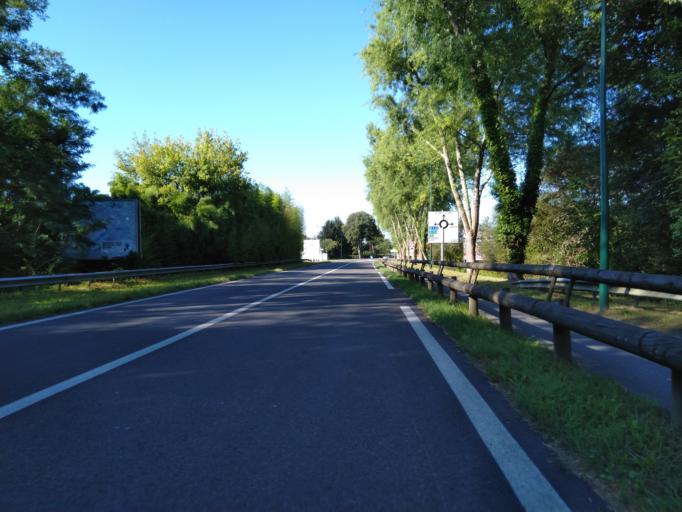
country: FR
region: Aquitaine
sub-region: Departement des Landes
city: Saint-Paul-les-Dax
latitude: 43.7318
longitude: -1.0350
